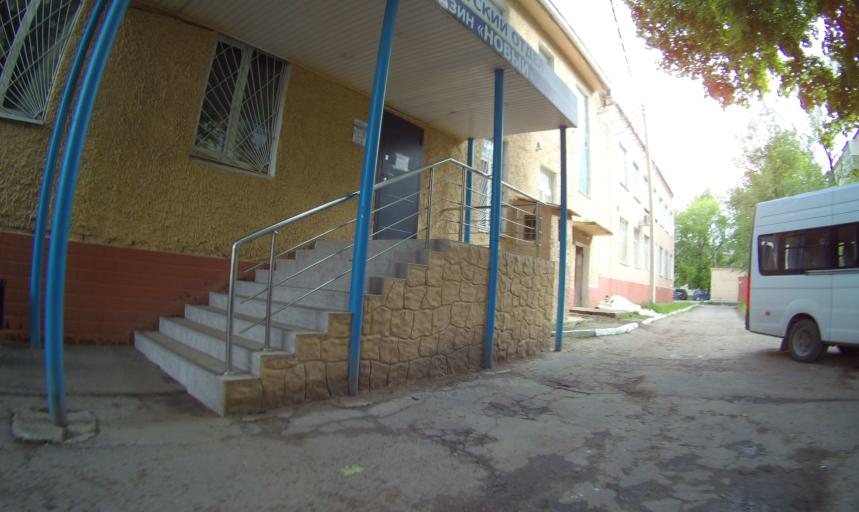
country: RU
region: Moskovskaya
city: Kolomna
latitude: 55.0905
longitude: 38.7703
